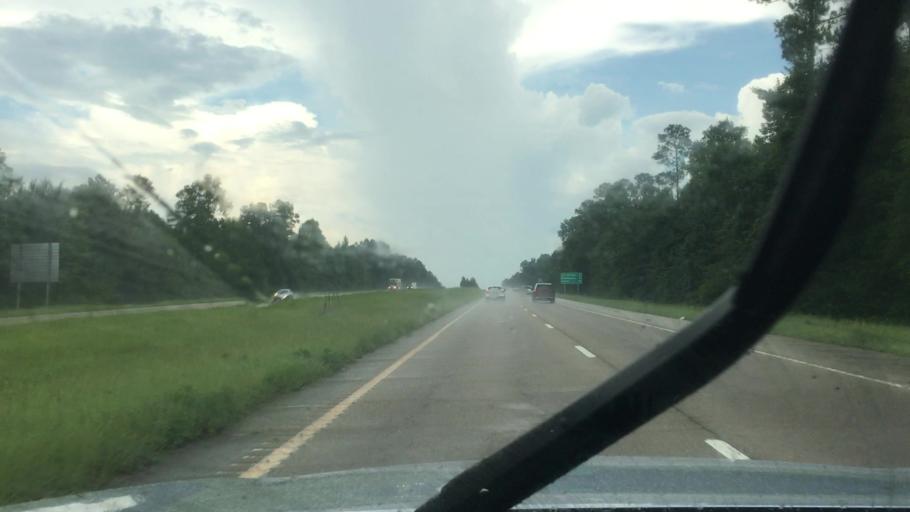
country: US
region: Mississippi
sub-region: Lamar County
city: Purvis
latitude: 31.1504
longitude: -89.3625
